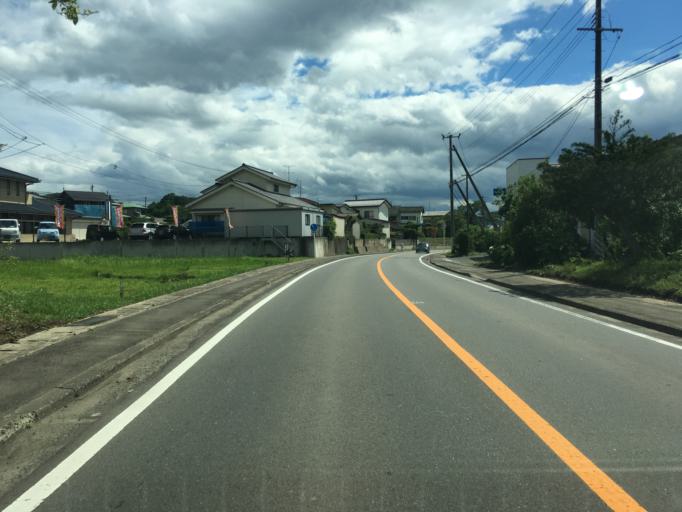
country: JP
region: Fukushima
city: Fukushima-shi
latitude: 37.6600
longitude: 140.5444
